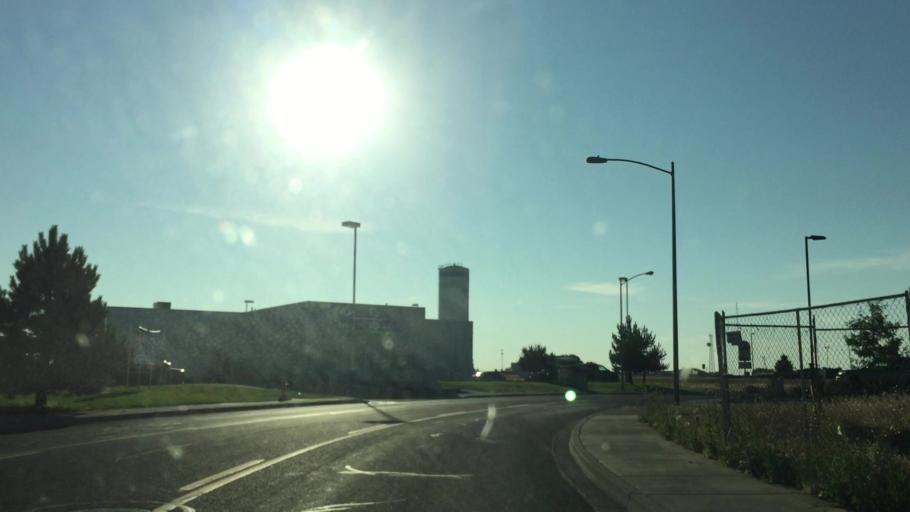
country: US
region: Washington
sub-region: Grant County
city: Moses Lake
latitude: 47.1039
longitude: -119.2517
